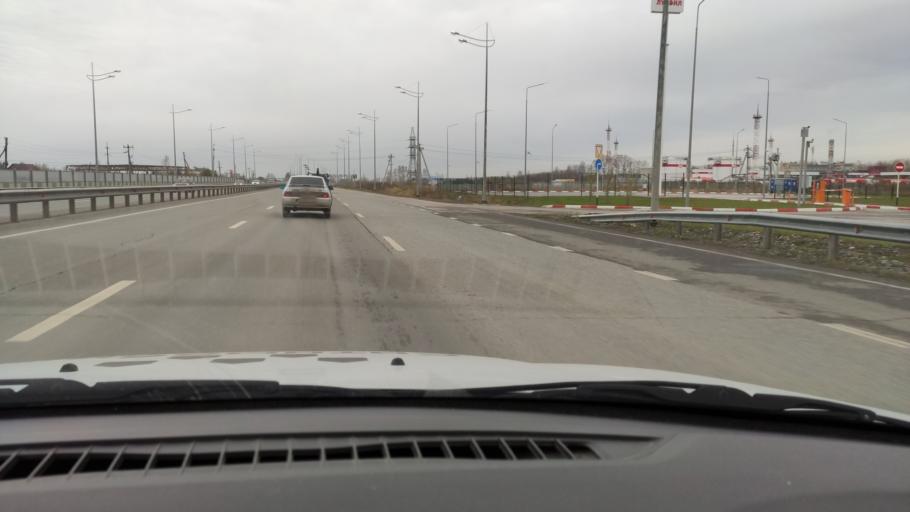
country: RU
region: Perm
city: Kultayevo
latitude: 57.9195
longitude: 56.0061
